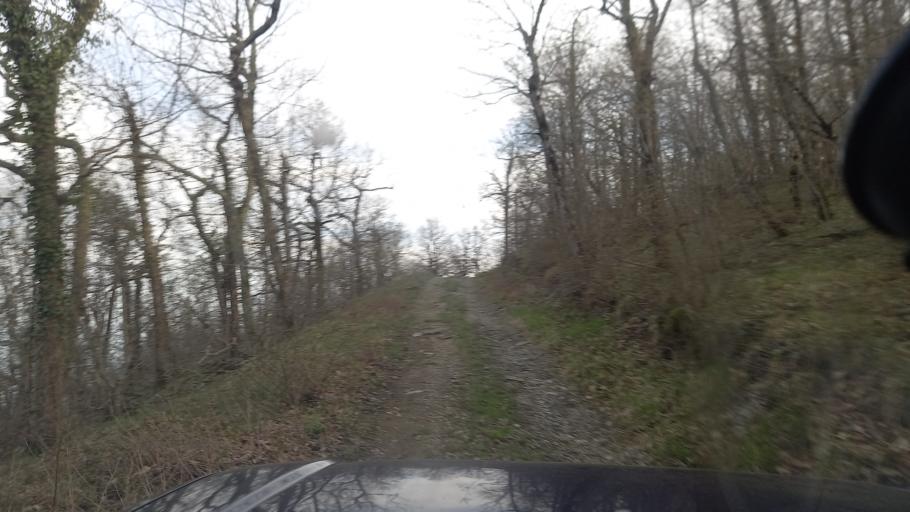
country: RU
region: Krasnodarskiy
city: Arkhipo-Osipovka
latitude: 44.3582
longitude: 38.5526
